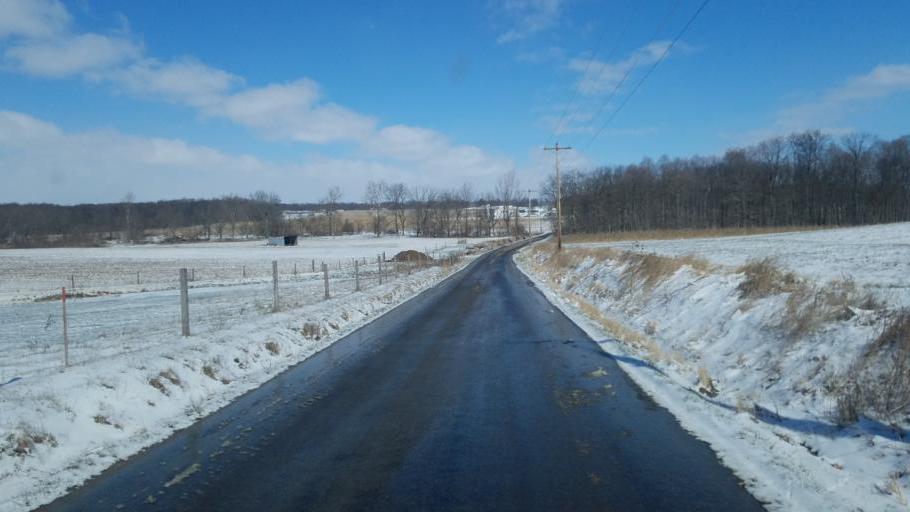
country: US
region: Ohio
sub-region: Knox County
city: Fredericktown
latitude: 40.5081
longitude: -82.6293
